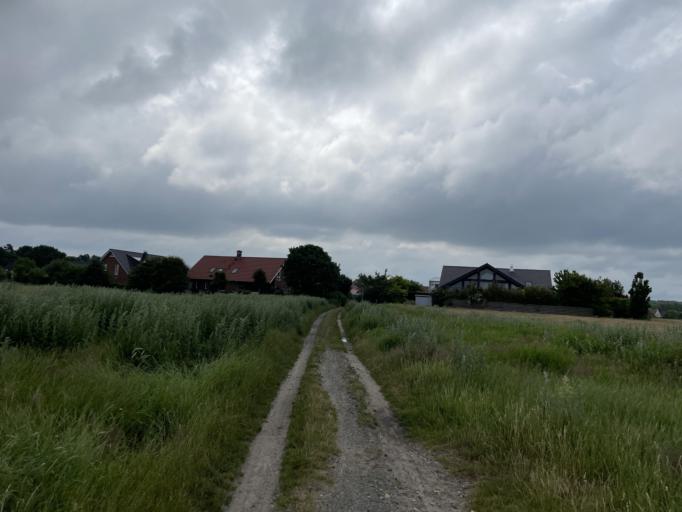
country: DE
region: Lower Saxony
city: Cuxhaven
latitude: 53.8761
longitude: 8.6479
